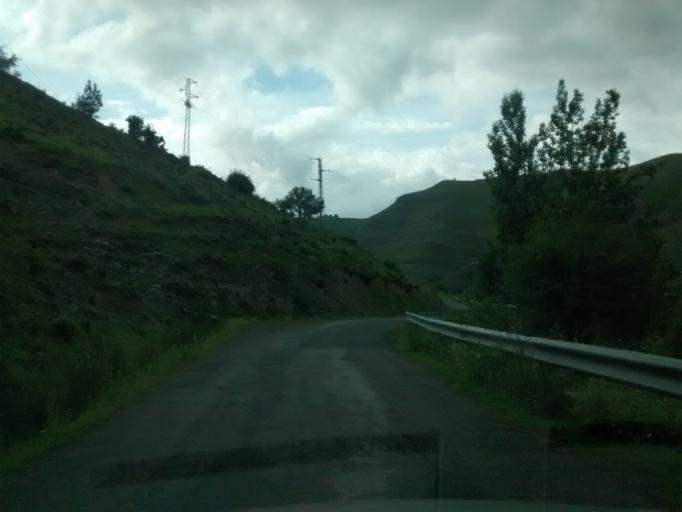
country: ES
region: La Rioja
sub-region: Provincia de La Rioja
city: San Roman de Cameros
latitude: 42.2164
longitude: -2.4652
